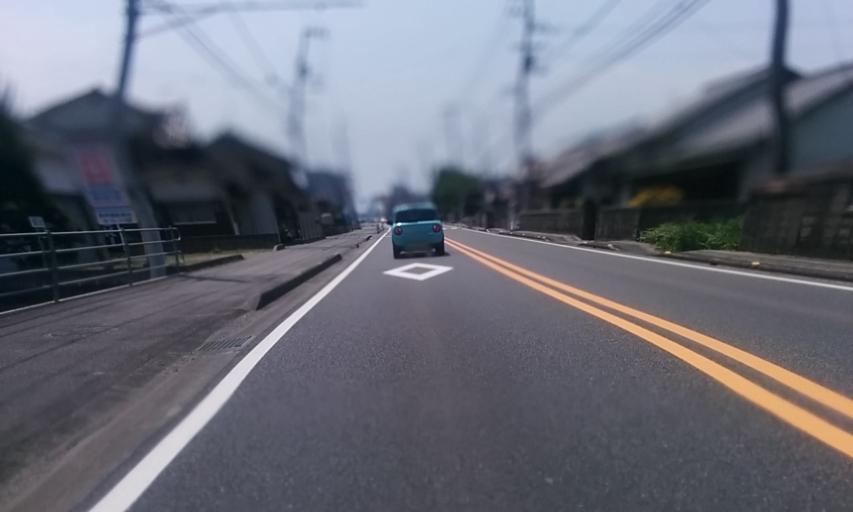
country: JP
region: Ehime
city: Saijo
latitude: 33.9103
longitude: 133.1965
